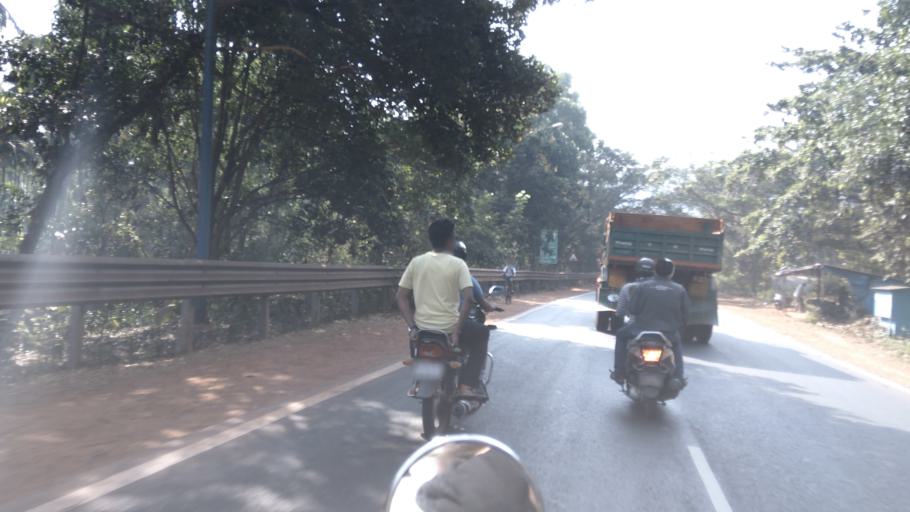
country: IN
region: Goa
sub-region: North Goa
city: Bandora
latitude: 15.4412
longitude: 73.9762
